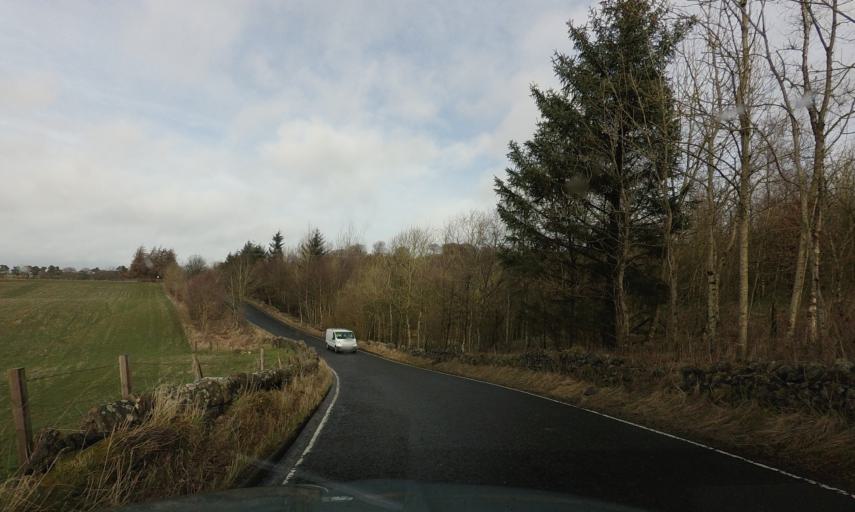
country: GB
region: Scotland
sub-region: West Lothian
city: Bathgate
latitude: 55.9327
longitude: -3.6245
